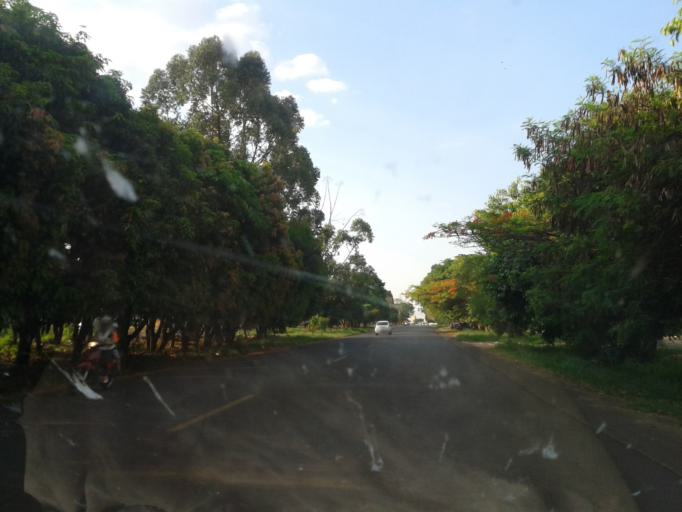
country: BR
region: Minas Gerais
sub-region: Uberlandia
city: Uberlandia
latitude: -18.9454
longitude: -48.3071
